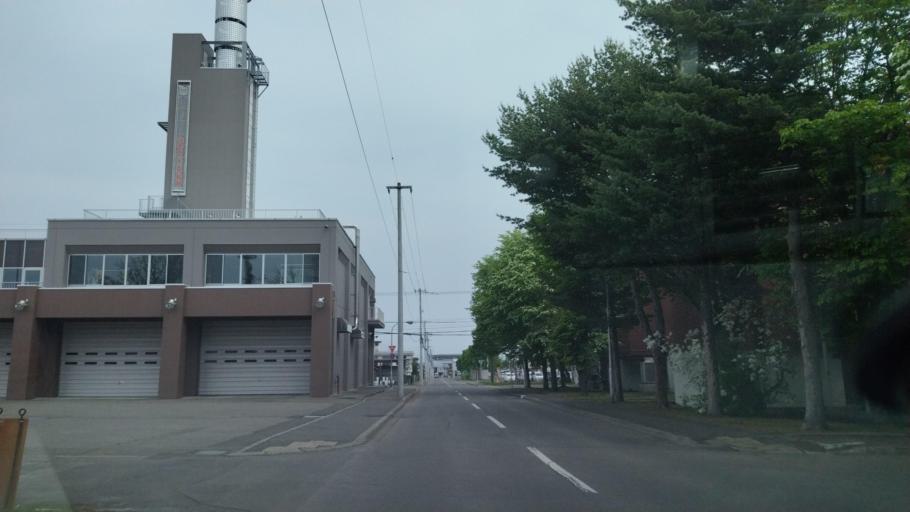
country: JP
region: Hokkaido
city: Obihiro
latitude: 42.9126
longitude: 143.0519
